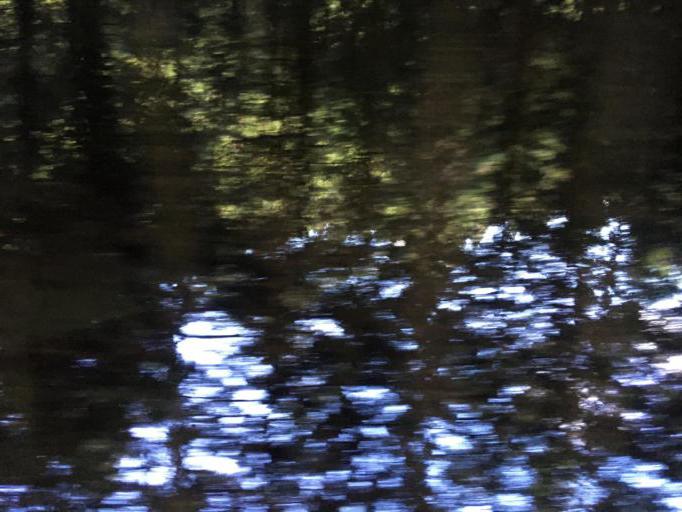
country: TW
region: Taiwan
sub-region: Yilan
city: Yilan
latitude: 24.5127
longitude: 121.5919
